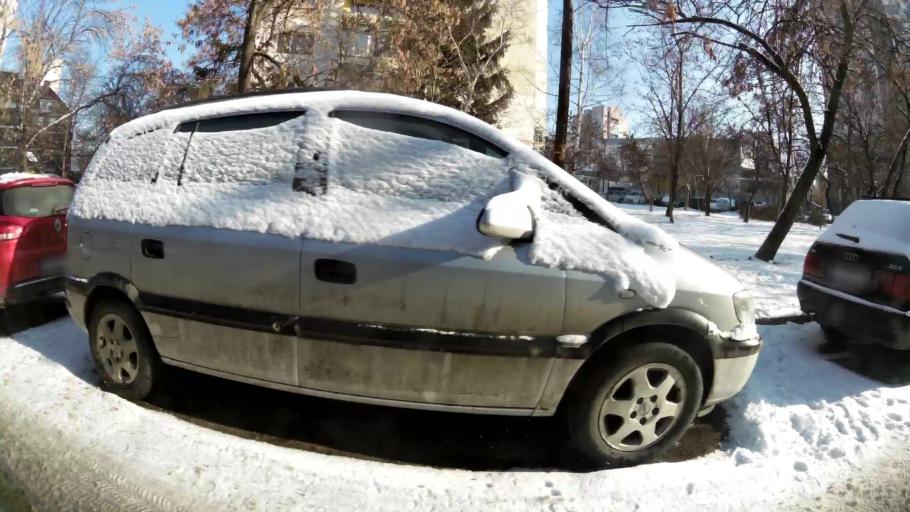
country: BG
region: Sofia-Capital
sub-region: Stolichna Obshtina
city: Sofia
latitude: 42.6591
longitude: 23.3402
